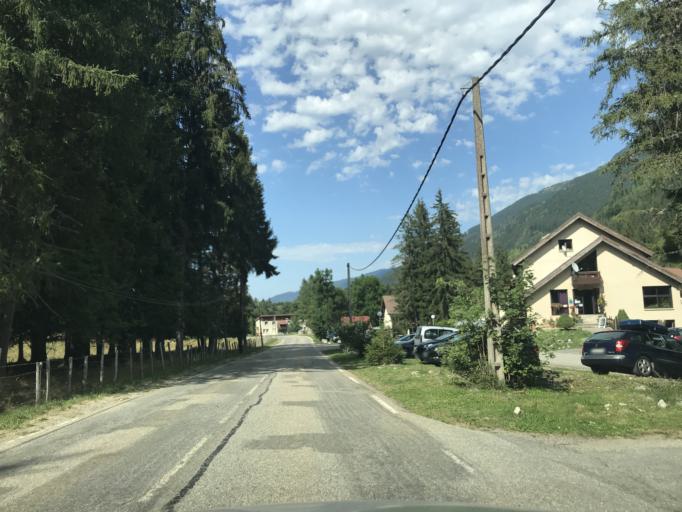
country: FR
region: Rhone-Alpes
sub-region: Departement de l'Isere
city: Theys
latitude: 45.2836
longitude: 6.0746
